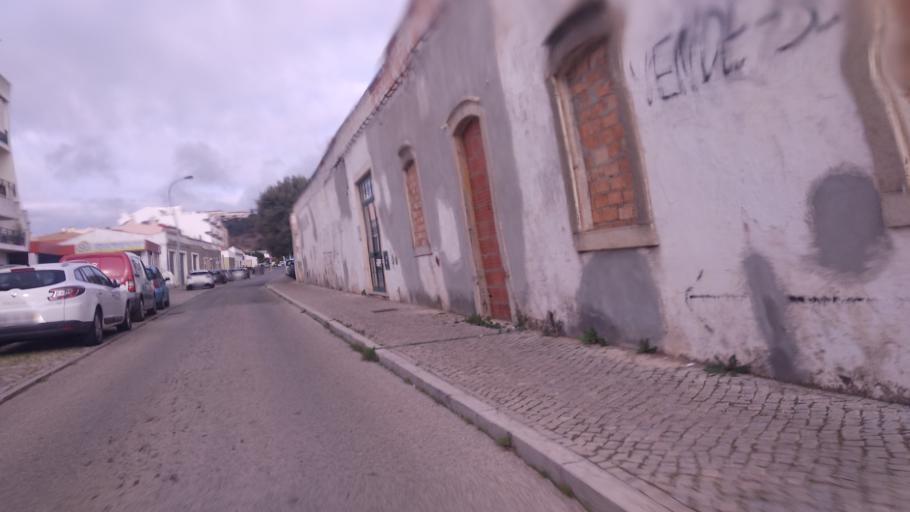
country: PT
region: Faro
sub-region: Sao Bras de Alportel
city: Sao Bras de Alportel
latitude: 37.1545
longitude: -7.8906
